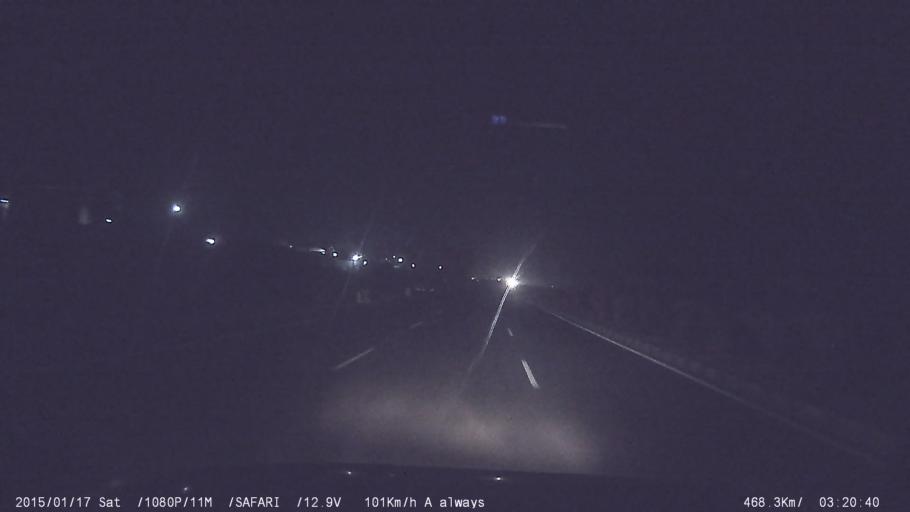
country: IN
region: Tamil Nadu
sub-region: Krishnagiri
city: Kelamangalam
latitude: 12.6694
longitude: 77.9885
